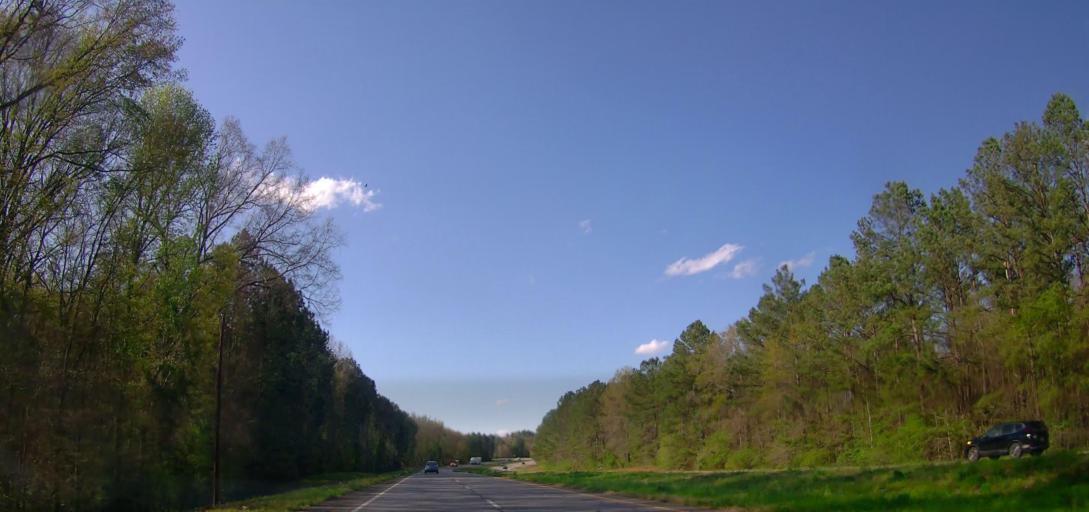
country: US
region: Georgia
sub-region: Baldwin County
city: Hardwick
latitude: 33.0398
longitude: -83.2541
